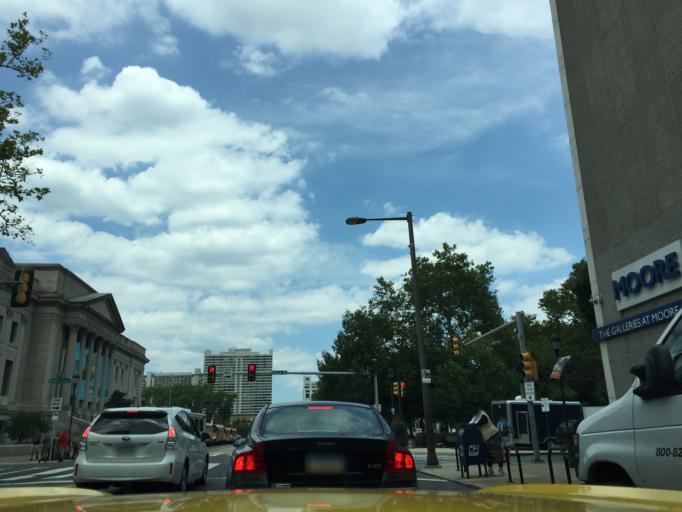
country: US
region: Pennsylvania
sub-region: Philadelphia County
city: Philadelphia
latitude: 39.9572
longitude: -75.1724
